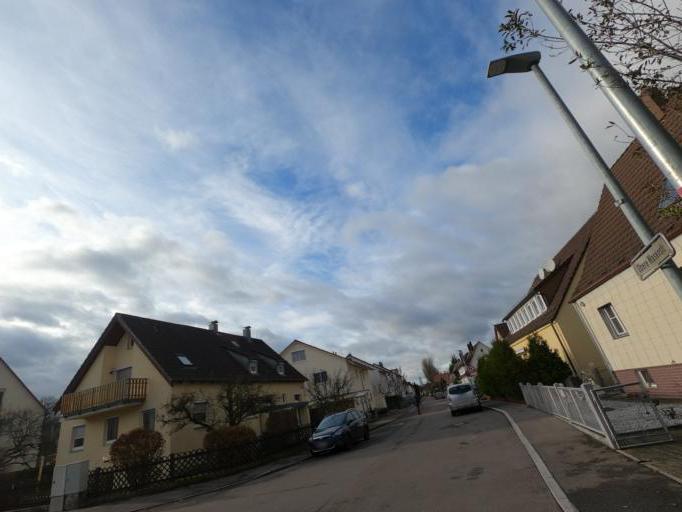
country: DE
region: Baden-Wuerttemberg
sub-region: Regierungsbezirk Stuttgart
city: Wangen
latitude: 48.7100
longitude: 9.6261
